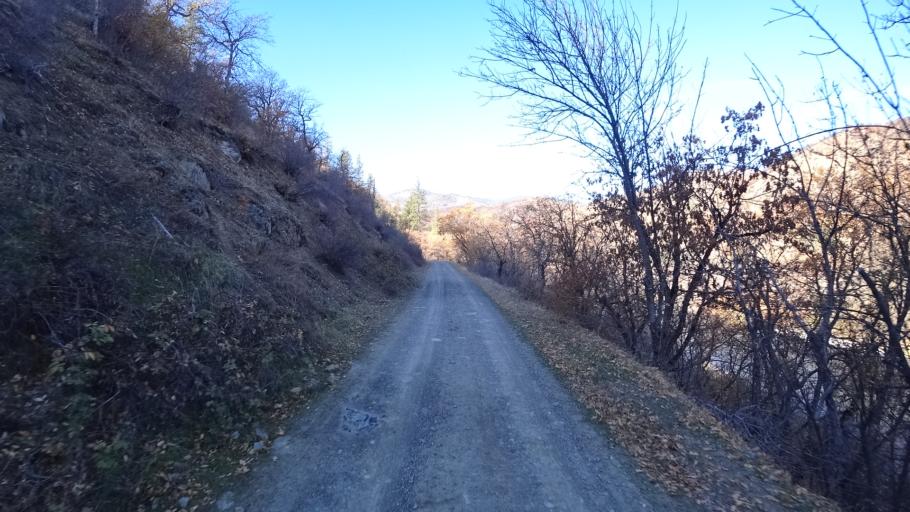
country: US
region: California
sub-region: Siskiyou County
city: Yreka
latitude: 41.8610
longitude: -122.7209
